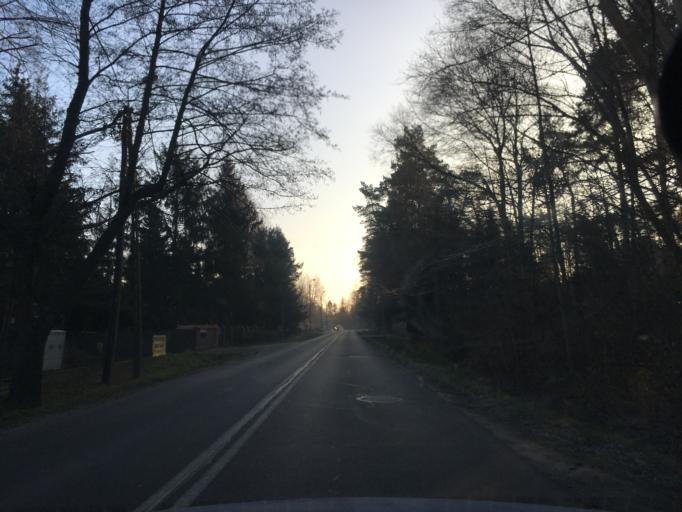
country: PL
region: Masovian Voivodeship
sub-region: Powiat piaseczynski
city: Piaseczno
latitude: 52.0707
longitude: 20.9809
